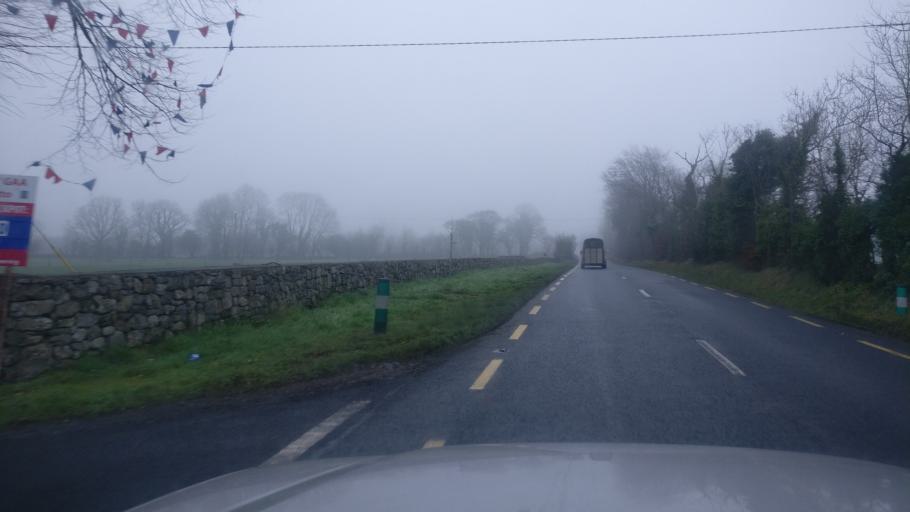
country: IE
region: Connaught
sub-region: County Galway
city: Gort
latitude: 53.1413
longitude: -8.7042
